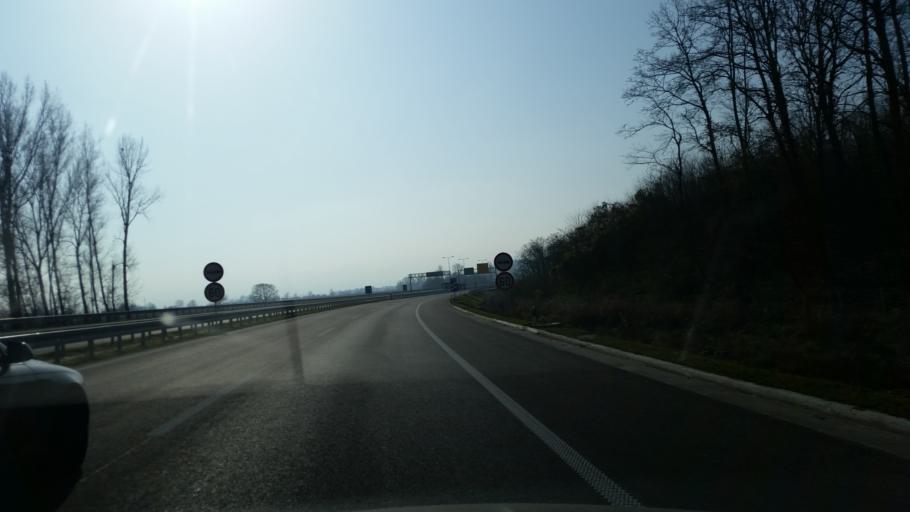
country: RS
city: Prislonica
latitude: 43.9273
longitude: 20.4014
